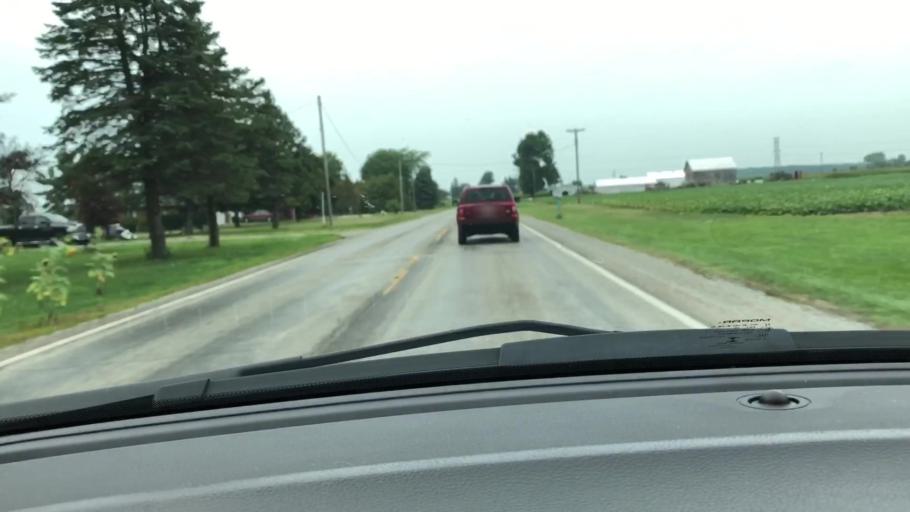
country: US
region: Michigan
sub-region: Saginaw County
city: Freeland
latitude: 43.5510
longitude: -84.0901
